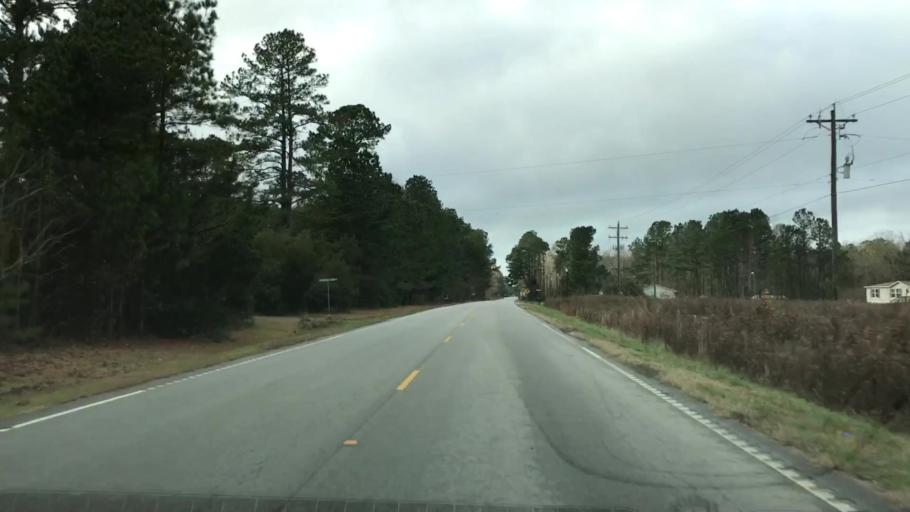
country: US
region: South Carolina
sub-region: Berkeley County
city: Saint Stephen
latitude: 33.2853
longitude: -79.7511
